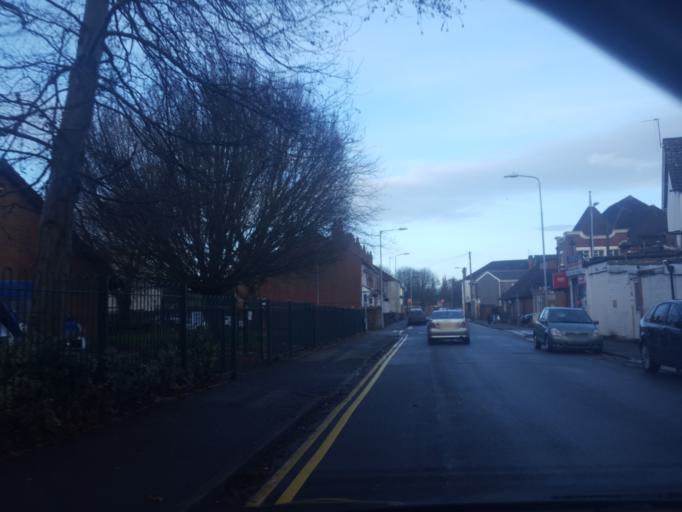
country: GB
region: England
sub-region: Wolverhampton
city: Wolverhampton
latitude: 52.5925
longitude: -2.1456
